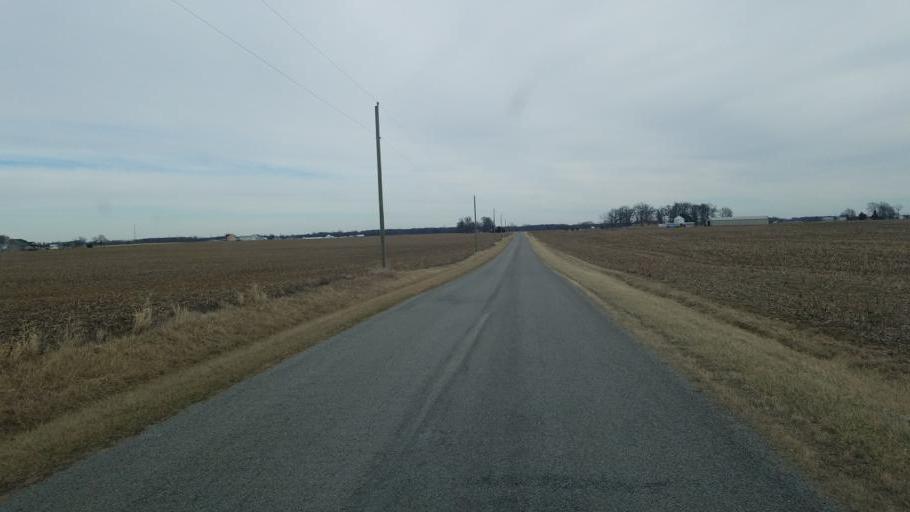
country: US
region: Ohio
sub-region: Union County
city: Richwood
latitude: 40.4961
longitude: -83.3563
